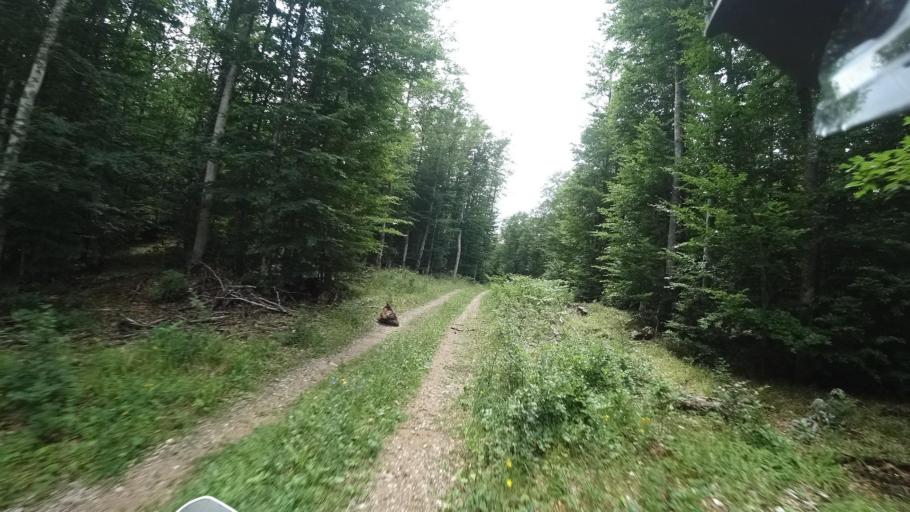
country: BA
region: Federation of Bosnia and Herzegovina
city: Bihac
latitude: 44.6377
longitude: 15.7828
